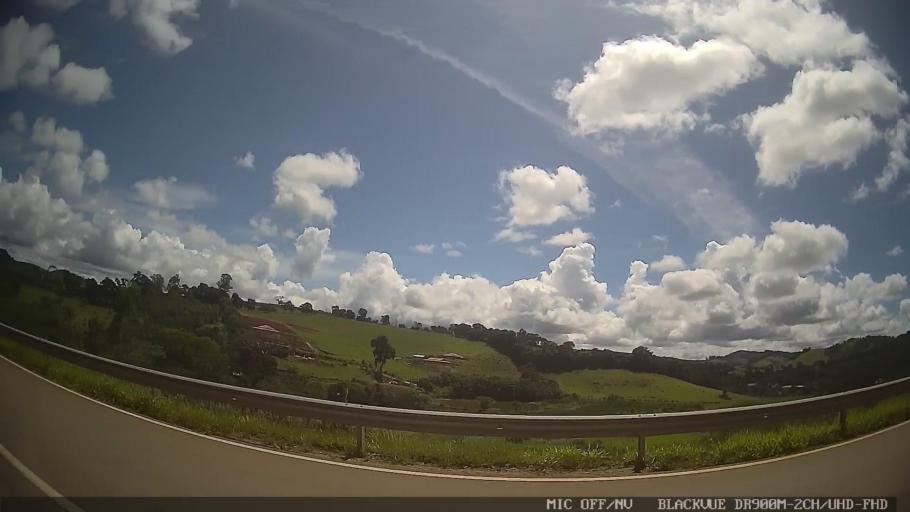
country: BR
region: Sao Paulo
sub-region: Amparo
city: Amparo
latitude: -22.8139
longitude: -46.6915
